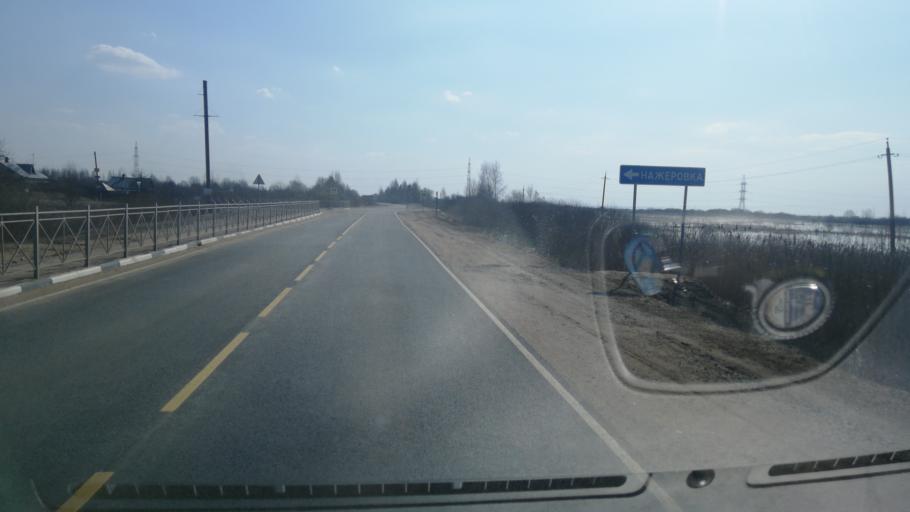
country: RU
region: Jaroslavl
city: Semibratovo
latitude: 57.2260
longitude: 39.5155
